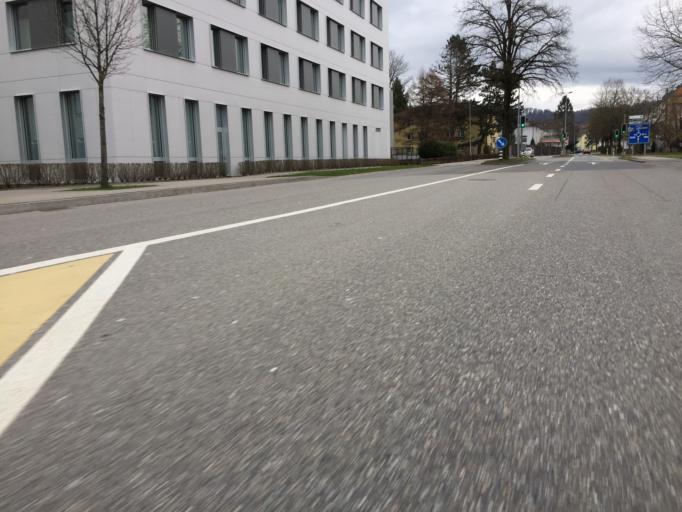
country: CH
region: Bern
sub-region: Emmental District
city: Burgdorf
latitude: 47.0638
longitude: 7.6136
